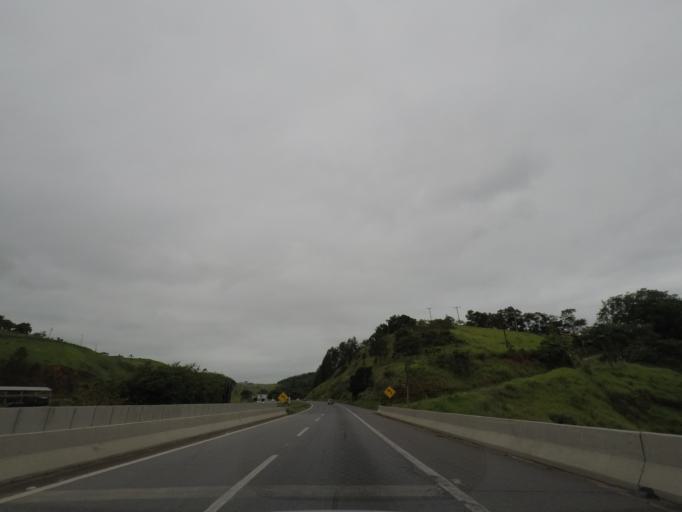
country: BR
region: Sao Paulo
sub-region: Santa Isabel
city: Santa Isabel
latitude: -23.2191
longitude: -46.1446
